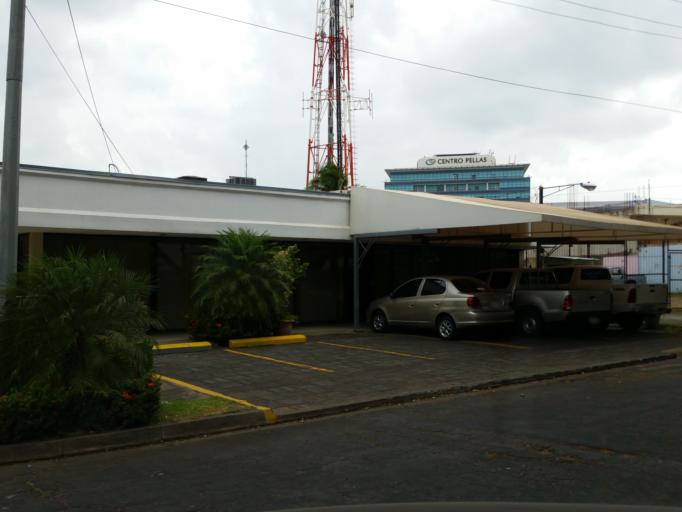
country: NI
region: Managua
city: Managua
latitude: 12.1203
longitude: -86.2633
